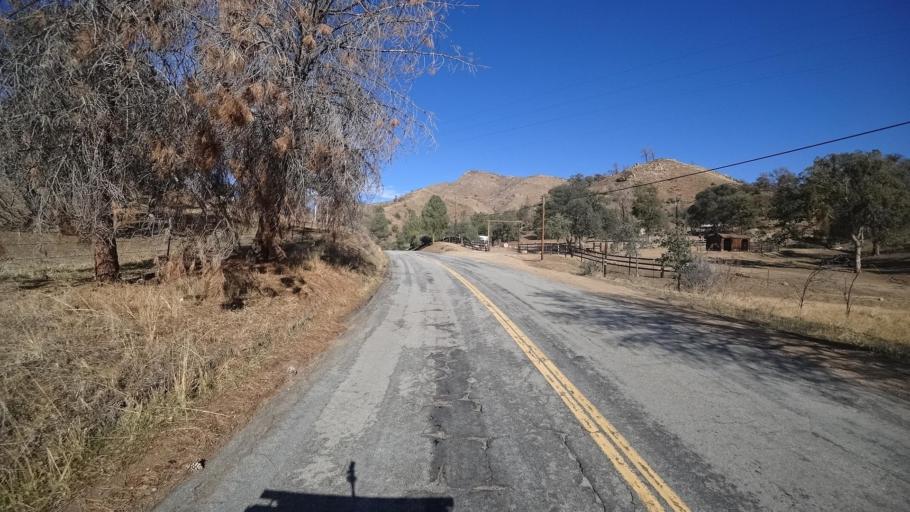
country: US
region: California
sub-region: Kern County
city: Bodfish
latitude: 35.4434
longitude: -118.5296
